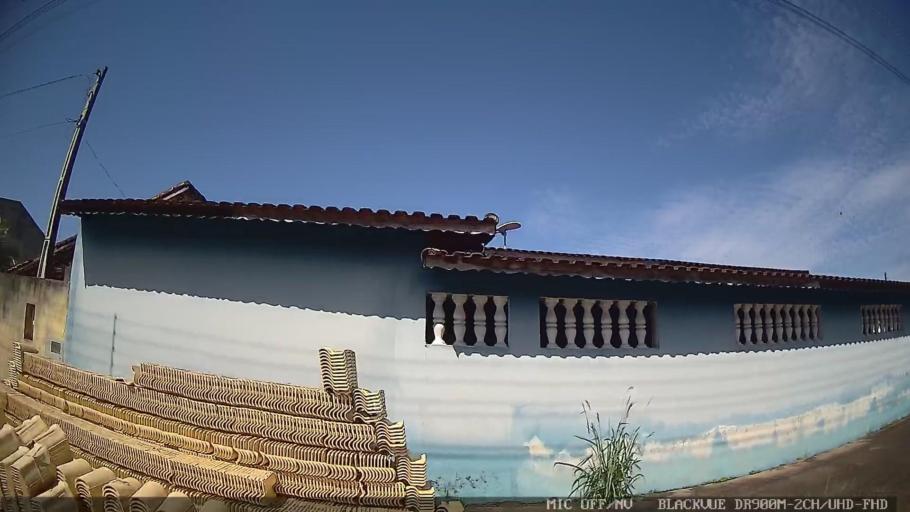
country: BR
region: Sao Paulo
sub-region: Itanhaem
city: Itanhaem
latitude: -24.1473
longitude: -46.7310
